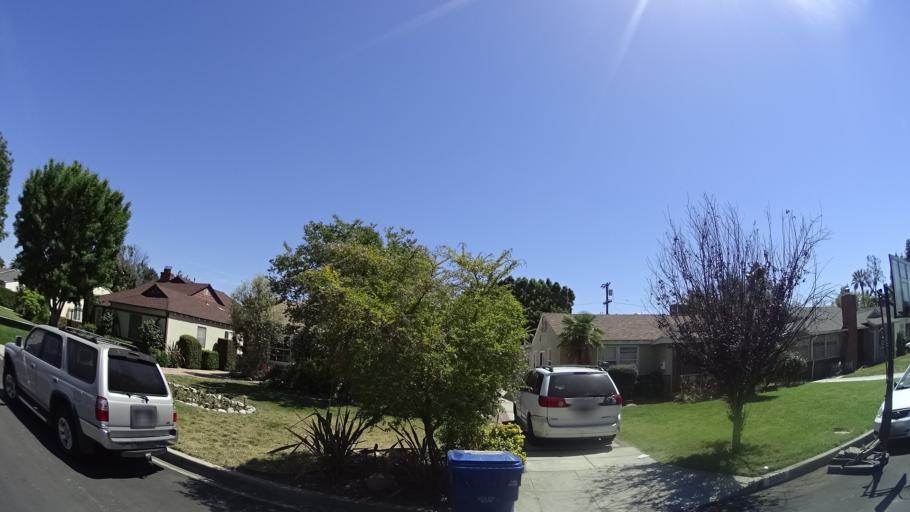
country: US
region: California
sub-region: Los Angeles County
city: North Hollywood
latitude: 34.1753
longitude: -118.4011
